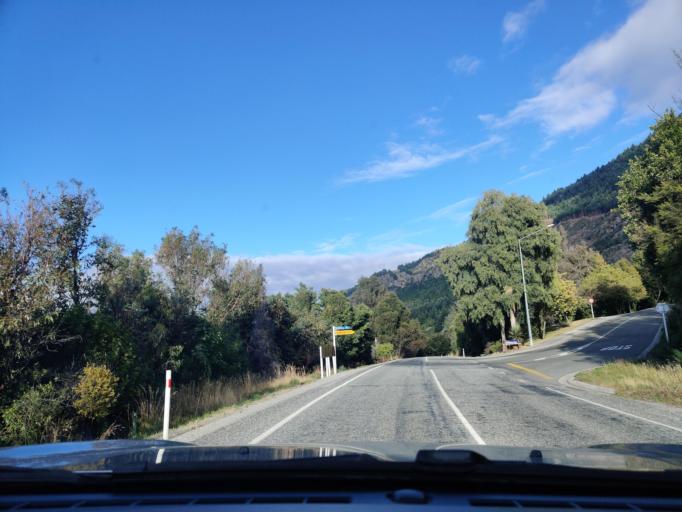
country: NZ
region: Otago
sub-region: Queenstown-Lakes District
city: Queenstown
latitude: -45.0463
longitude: 168.6298
